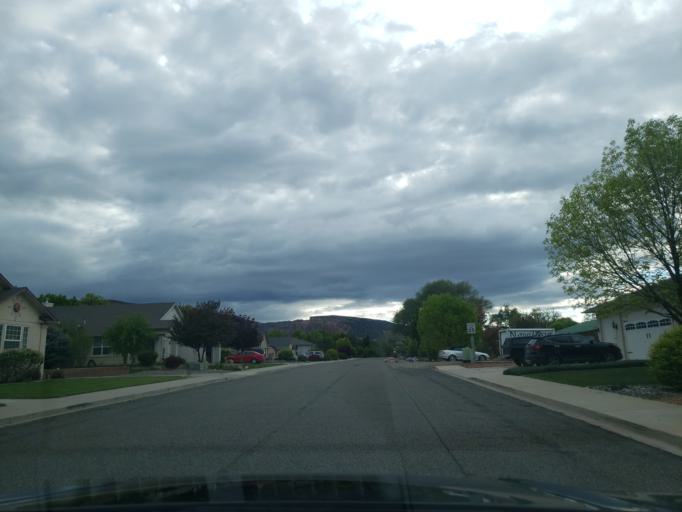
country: US
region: Colorado
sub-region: Mesa County
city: Redlands
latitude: 39.1033
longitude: -108.6696
